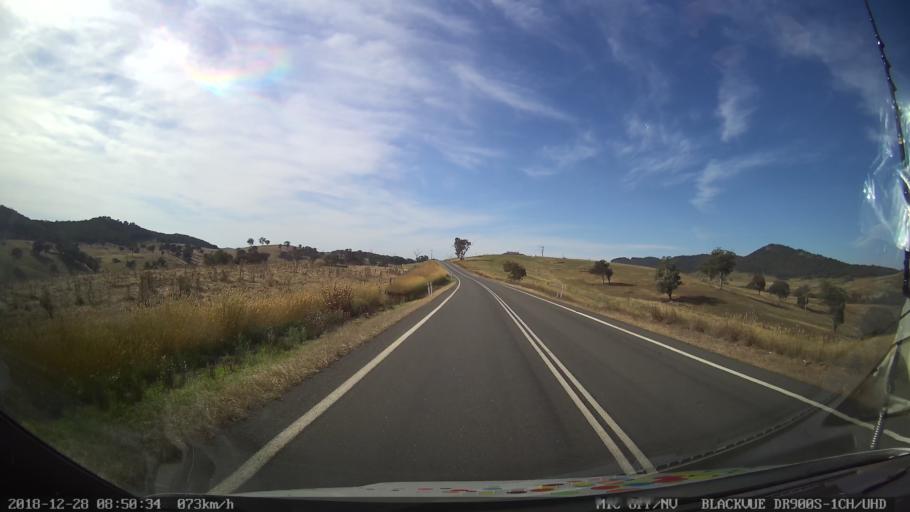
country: AU
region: New South Wales
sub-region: Upper Lachlan Shire
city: Crookwell
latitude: -34.0590
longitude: 149.3379
